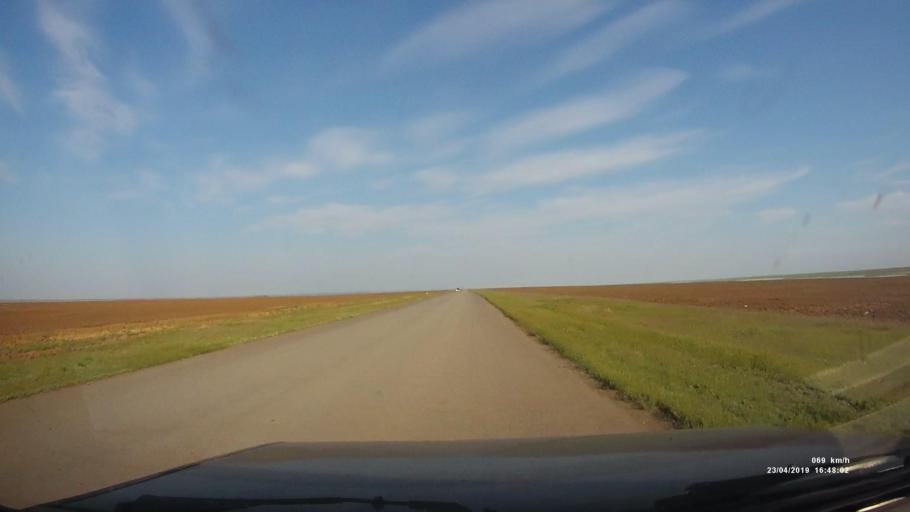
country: RU
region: Kalmykiya
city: Priyutnoye
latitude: 46.3365
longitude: 43.2560
